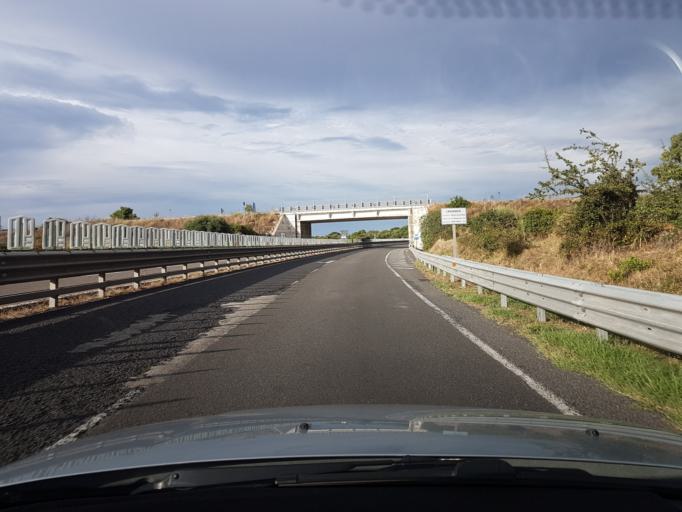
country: IT
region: Sardinia
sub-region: Provincia di Oristano
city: Paulilatino
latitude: 40.0896
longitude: 8.7563
